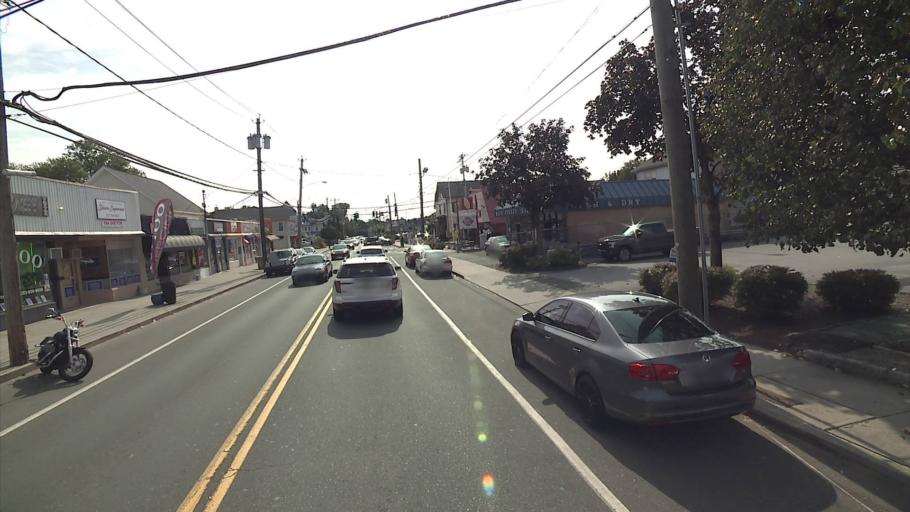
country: US
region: Connecticut
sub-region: Fairfield County
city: Norwalk
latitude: 41.1261
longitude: -73.4202
